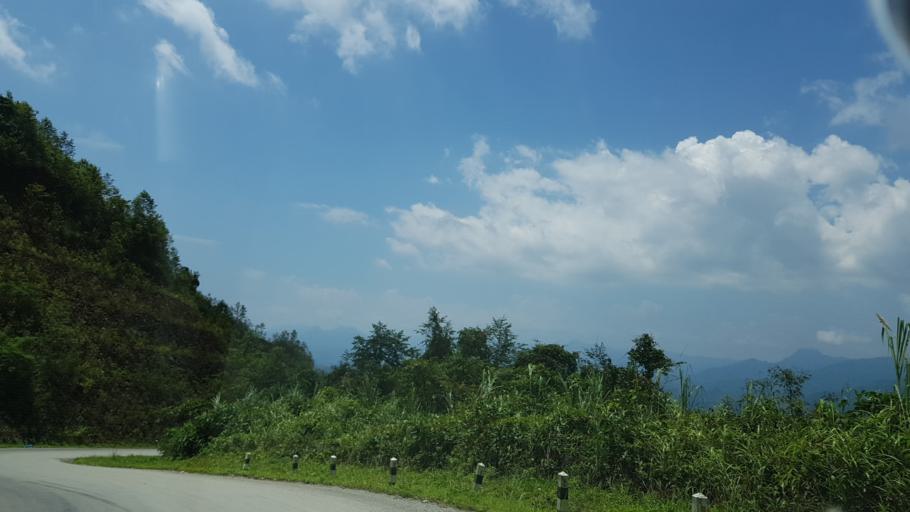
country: LA
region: Vientiane
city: Muang Kasi
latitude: 19.3820
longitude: 102.1540
